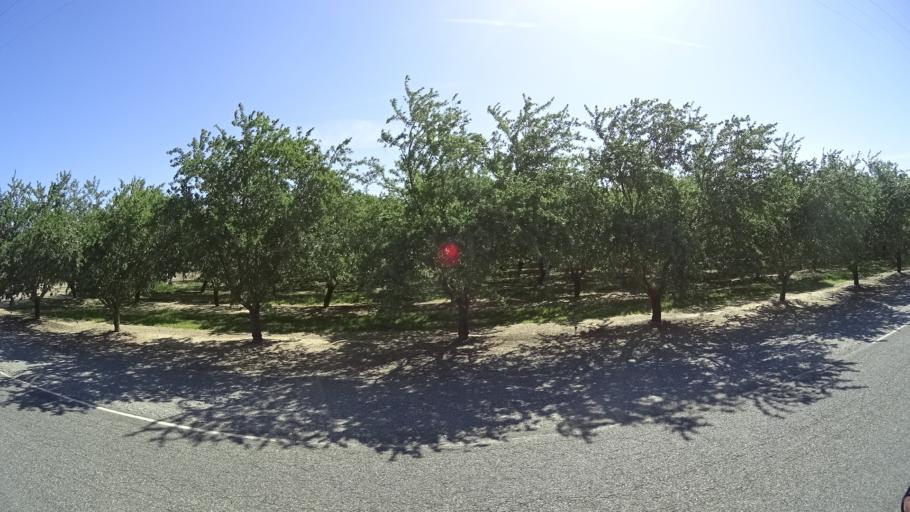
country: US
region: California
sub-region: Glenn County
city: Willows
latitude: 39.6311
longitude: -122.1787
